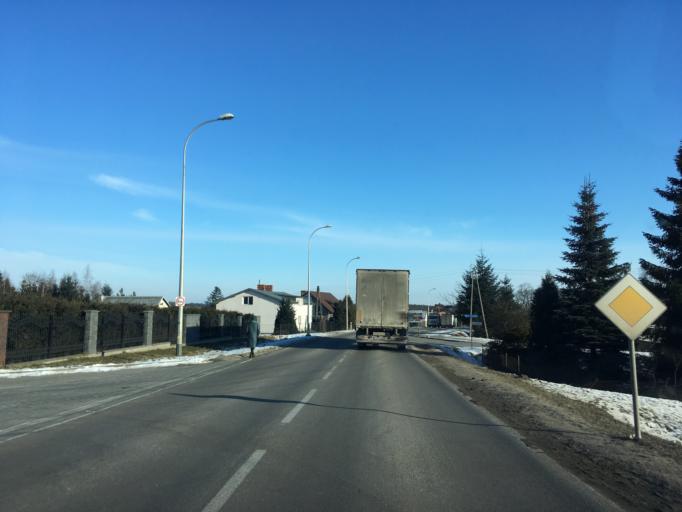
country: PL
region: Pomeranian Voivodeship
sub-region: Powiat starogardzki
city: Zblewo
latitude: 53.9408
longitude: 18.3227
